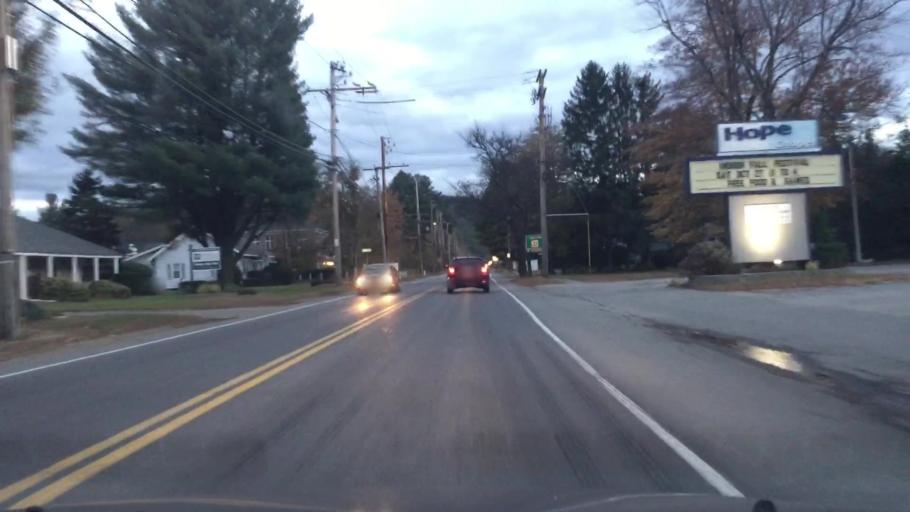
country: US
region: New Hampshire
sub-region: Cheshire County
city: Keene
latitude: 42.9134
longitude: -72.2671
